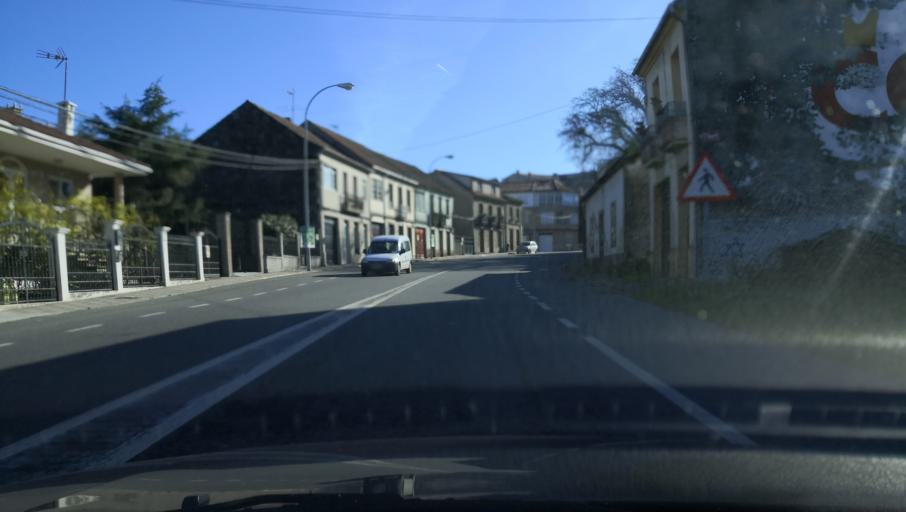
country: ES
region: Galicia
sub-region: Provincia de Pontevedra
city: Silleda
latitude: 42.7315
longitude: -8.3070
